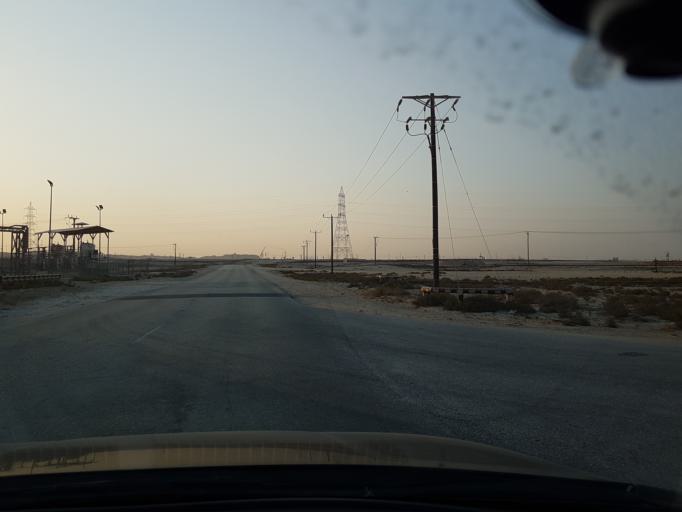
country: BH
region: Central Governorate
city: Dar Kulayb
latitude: 26.0168
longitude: 50.5756
